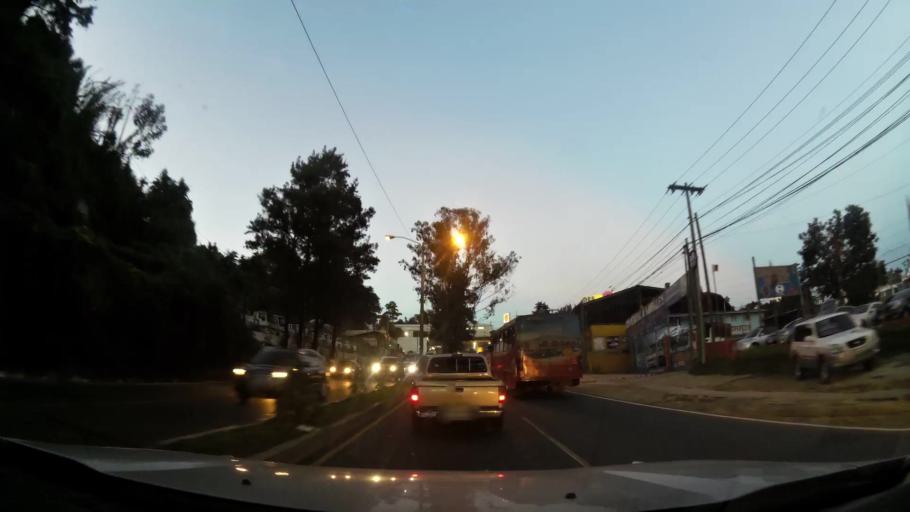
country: GT
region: Guatemala
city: Mixco
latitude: 14.6341
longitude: -90.5992
